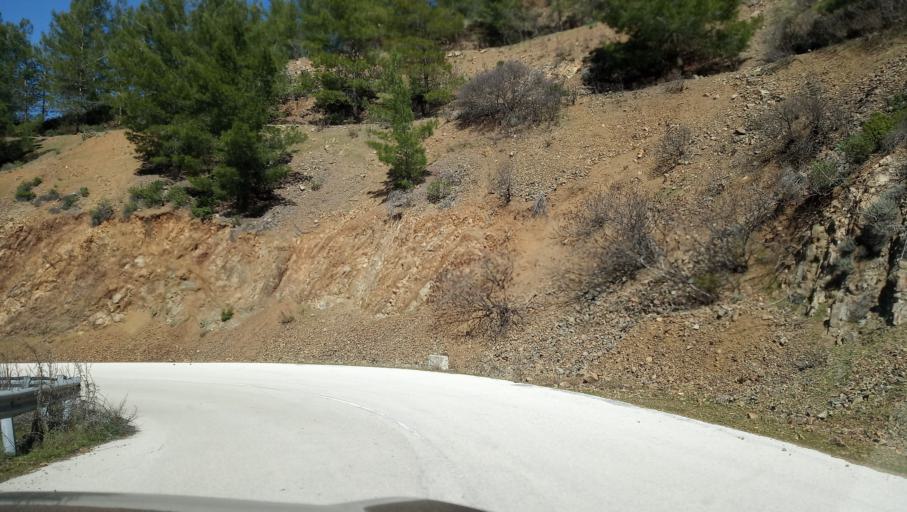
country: CY
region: Lefkosia
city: Lefka
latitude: 35.0614
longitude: 32.7470
